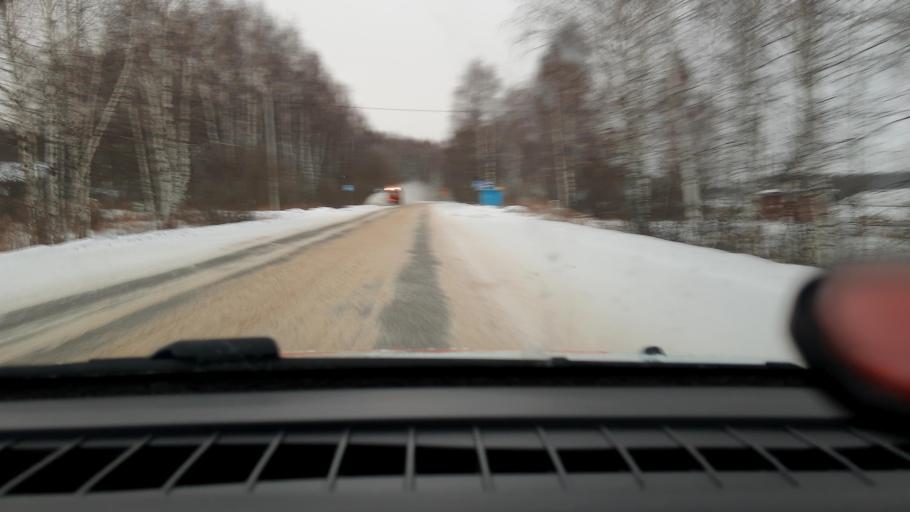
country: RU
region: Nizjnij Novgorod
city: Pamyat' Parizhskoy Kommuny
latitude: 56.2502
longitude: 44.4803
